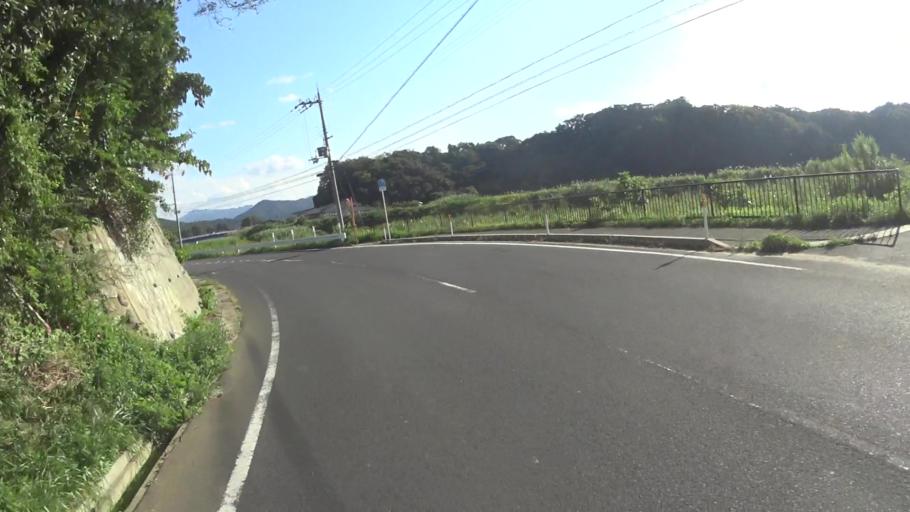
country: JP
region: Hyogo
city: Toyooka
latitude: 35.6433
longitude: 134.9447
